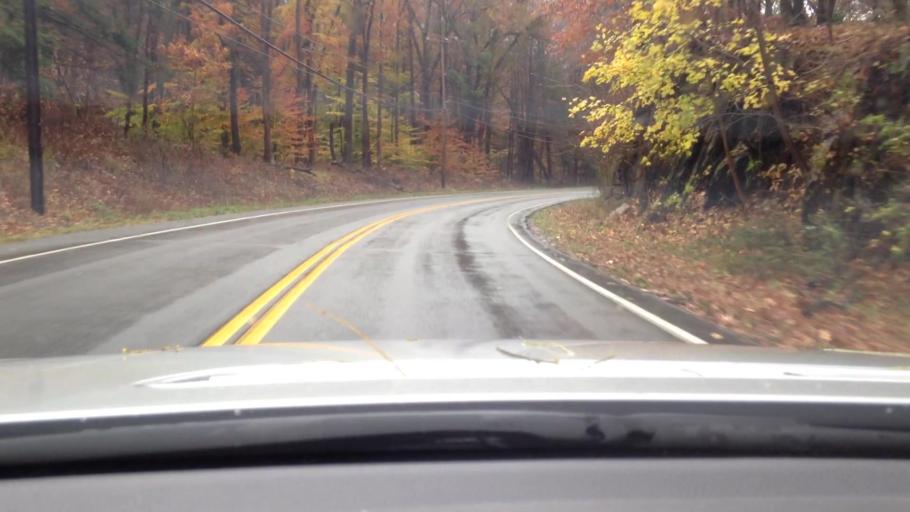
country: US
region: New York
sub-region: Orange County
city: West Point
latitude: 41.4038
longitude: -73.9306
